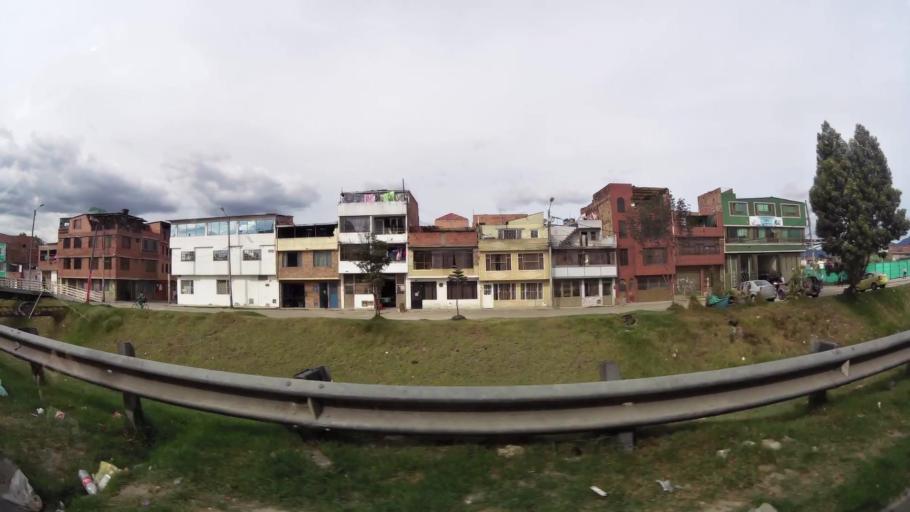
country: CO
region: Cundinamarca
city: Soacha
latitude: 4.6410
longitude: -74.1677
